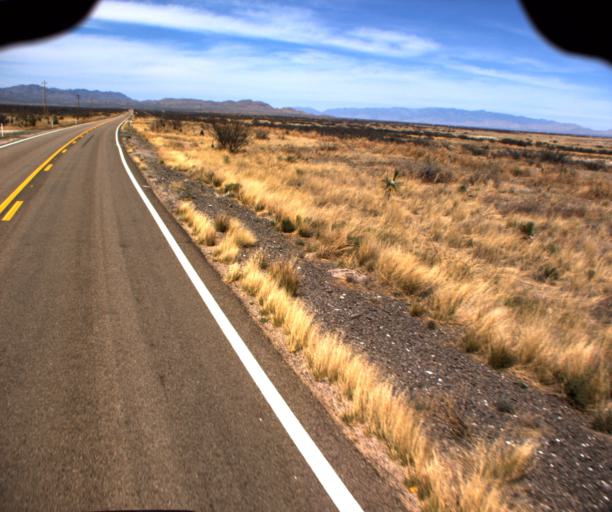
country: US
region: Arizona
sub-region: Cochise County
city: Willcox
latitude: 32.1457
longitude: -109.9337
